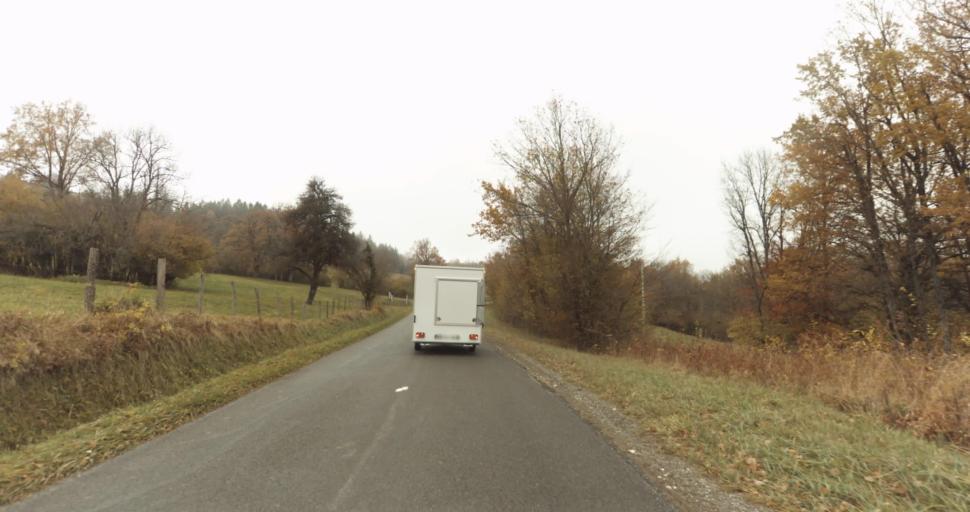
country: FR
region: Rhone-Alpes
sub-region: Departement de la Haute-Savoie
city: Groisy
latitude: 46.0202
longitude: 6.1779
